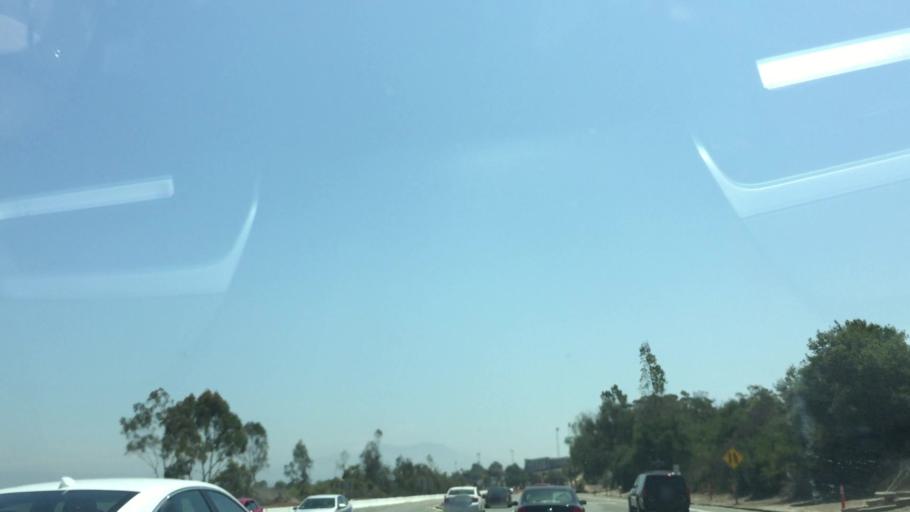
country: US
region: California
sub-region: Orange County
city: Irvine
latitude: 33.6503
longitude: -117.8584
